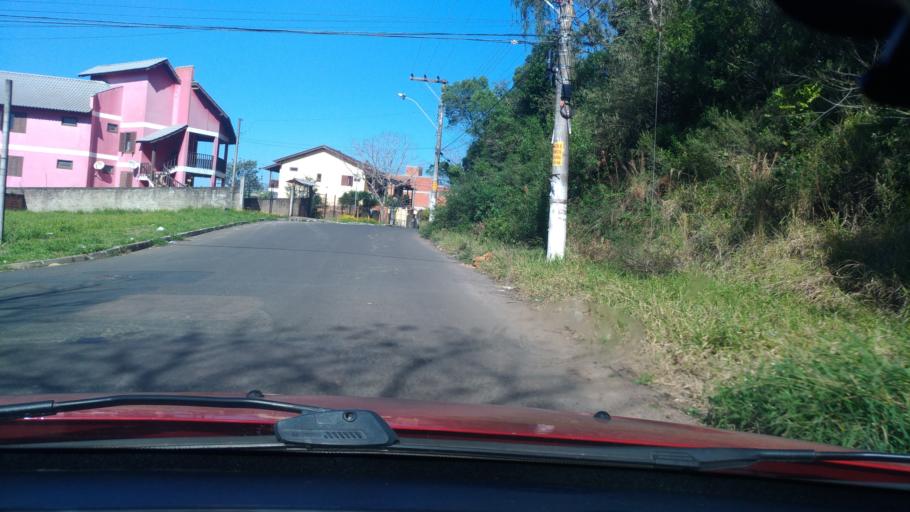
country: BR
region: Rio Grande do Sul
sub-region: Viamao
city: Viamao
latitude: -30.0538
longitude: -51.1041
